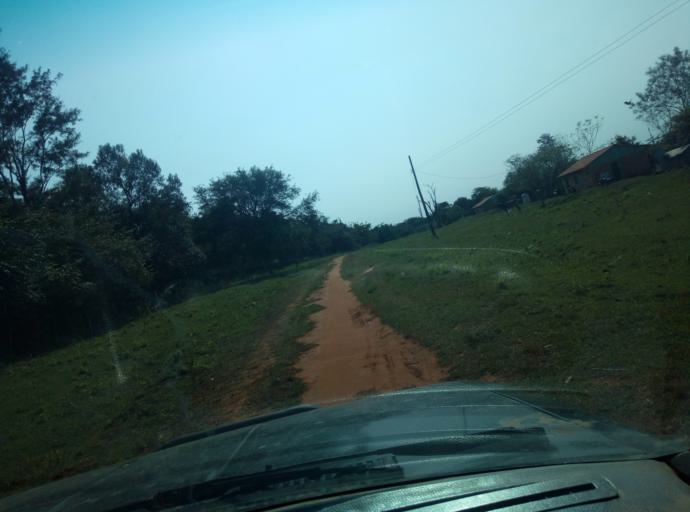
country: PY
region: Caaguazu
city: Carayao
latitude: -25.3051
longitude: -56.3246
